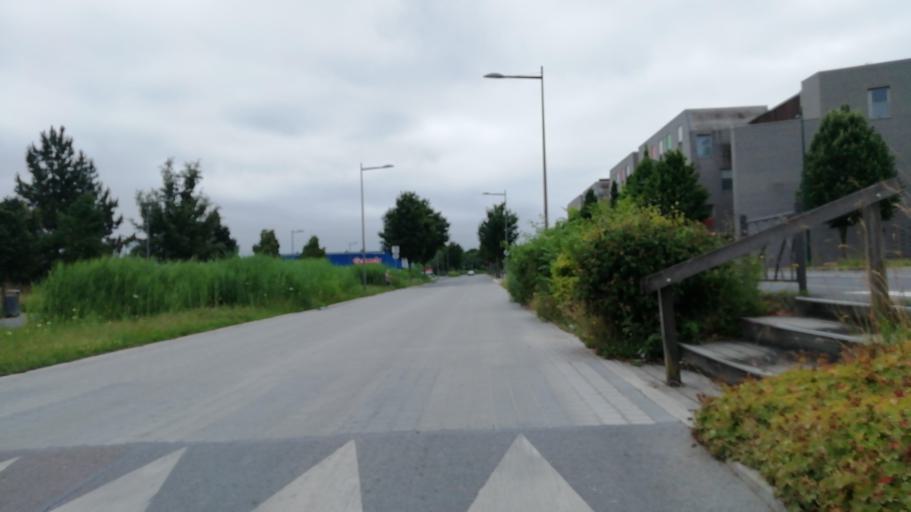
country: FR
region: Champagne-Ardenne
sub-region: Departement de la Marne
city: Betheny
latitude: 49.2603
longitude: 4.0625
